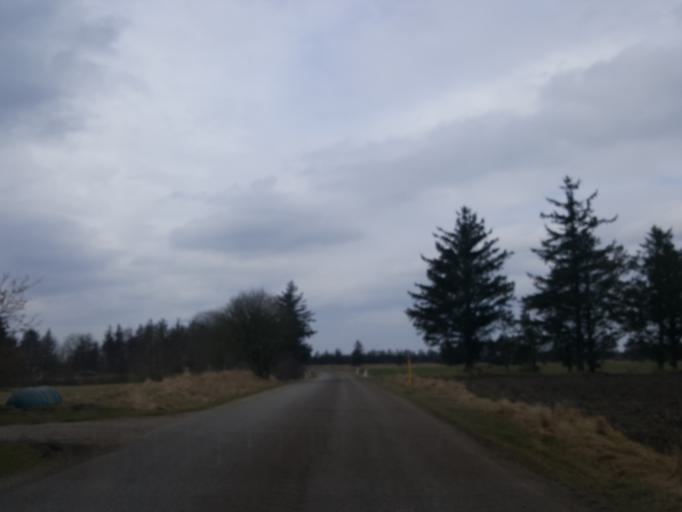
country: DK
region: Central Jutland
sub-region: Holstebro Kommune
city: Ulfborg
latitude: 56.3493
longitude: 8.2994
